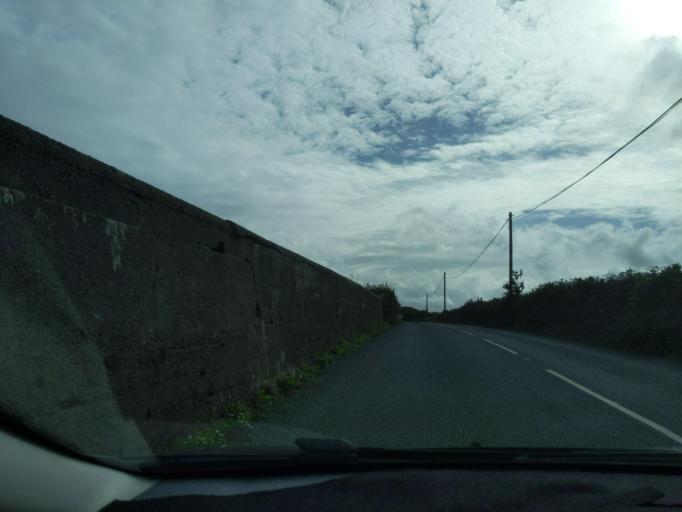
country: GB
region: England
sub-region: Cornwall
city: Mevagissey
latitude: 50.2717
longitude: -4.8293
